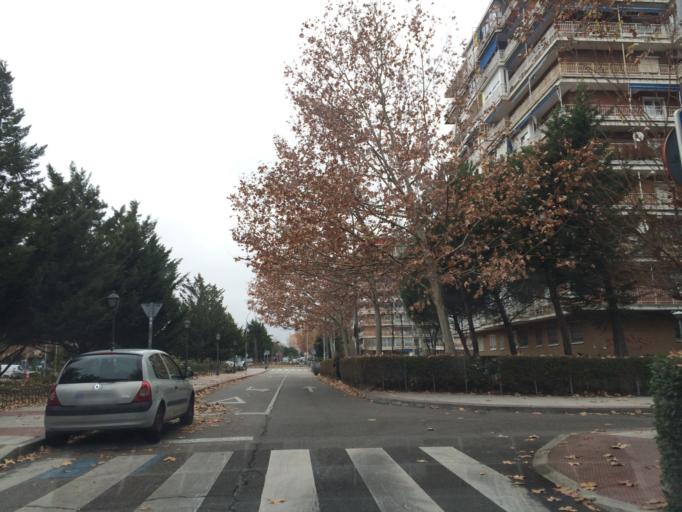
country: ES
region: Madrid
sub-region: Provincia de Madrid
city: Alcorcon
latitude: 40.3488
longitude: -3.8195
